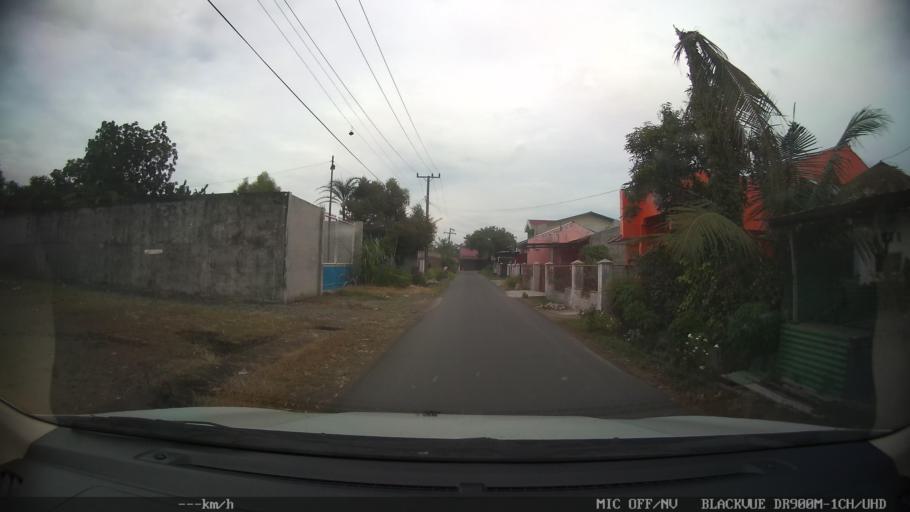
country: ID
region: North Sumatra
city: Sunggal
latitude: 3.6198
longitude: 98.5924
